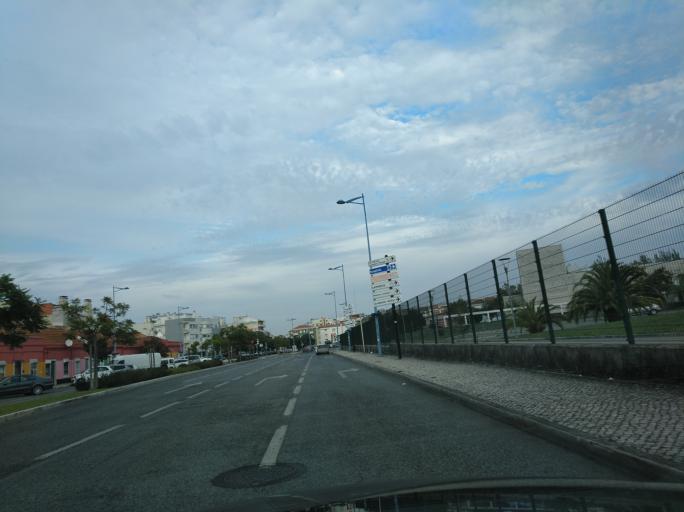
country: PT
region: Lisbon
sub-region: Amadora
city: Amadora
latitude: 38.7557
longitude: -9.2366
